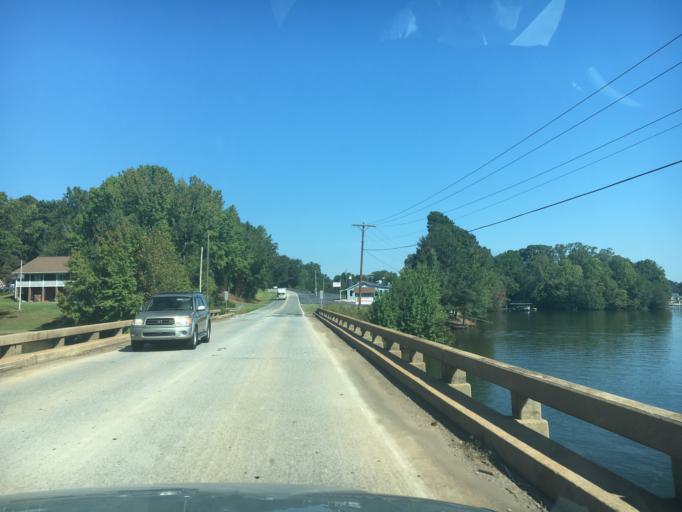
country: US
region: South Carolina
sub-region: Spartanburg County
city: Inman
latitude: 35.1135
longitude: -82.0406
